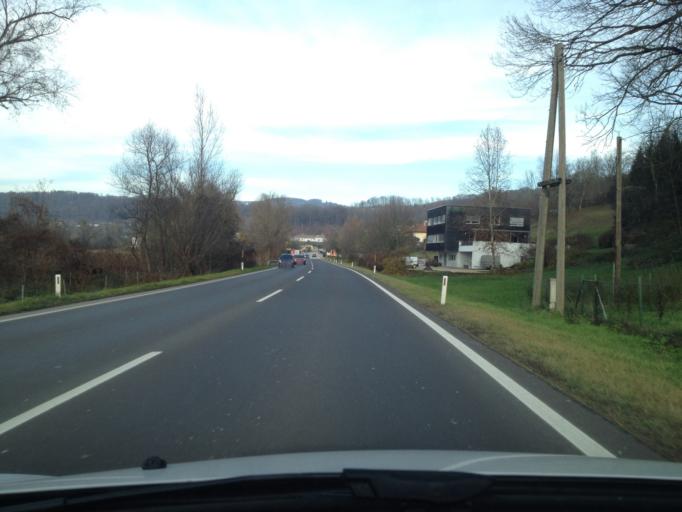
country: AT
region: Upper Austria
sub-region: Politischer Bezirk Urfahr-Umgebung
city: Steyregg
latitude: 48.3160
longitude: 14.3374
